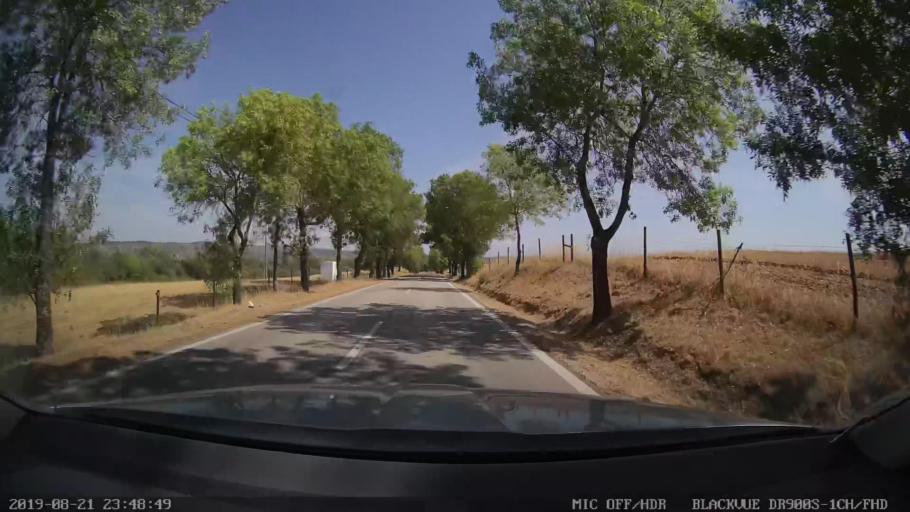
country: PT
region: Castelo Branco
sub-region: Idanha-A-Nova
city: Idanha-a-Nova
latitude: 39.8702
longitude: -7.2535
